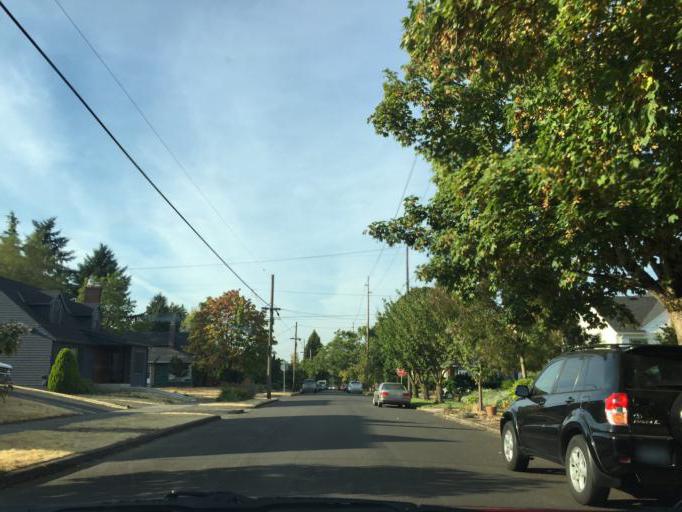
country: US
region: Oregon
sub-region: Multnomah County
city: Portland
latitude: 45.5593
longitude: -122.6297
